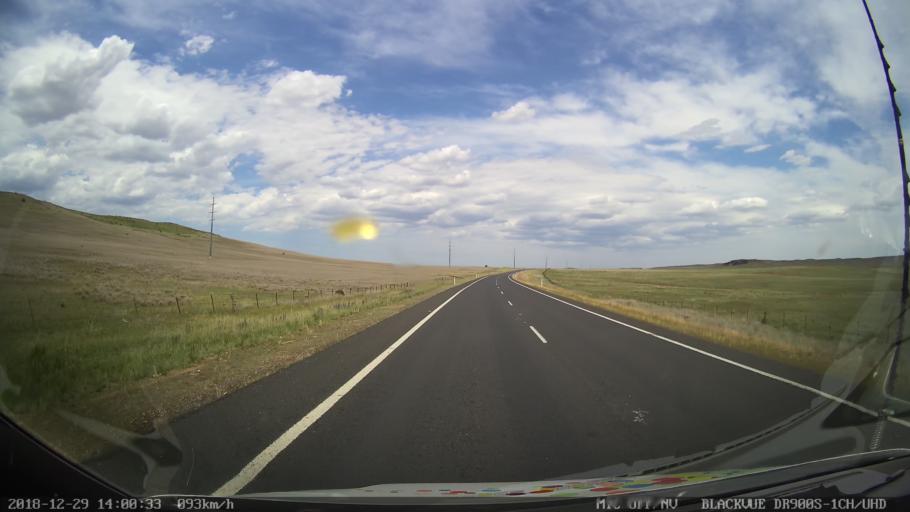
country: AU
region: New South Wales
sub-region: Cooma-Monaro
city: Cooma
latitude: -36.2647
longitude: 149.1601
